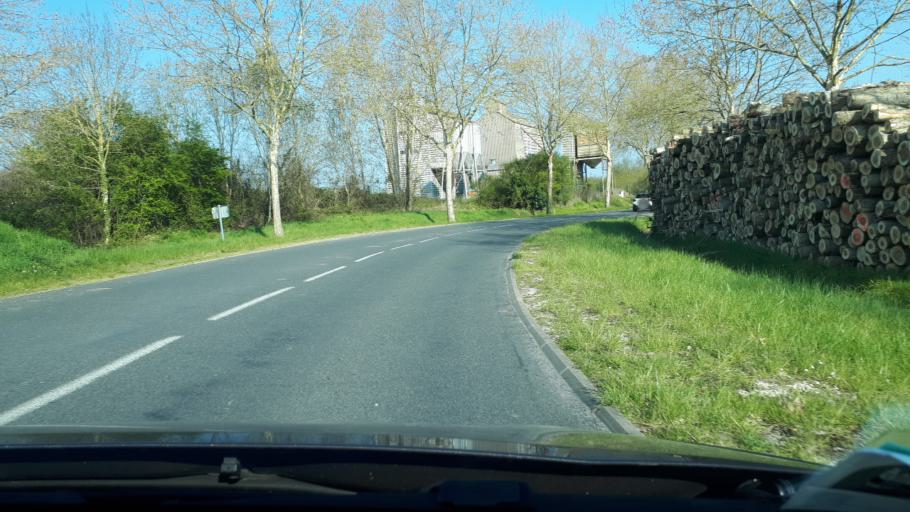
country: FR
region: Centre
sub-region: Departement d'Indre-et-Loire
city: La Croix-en-Touraine
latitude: 47.3383
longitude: 0.9832
